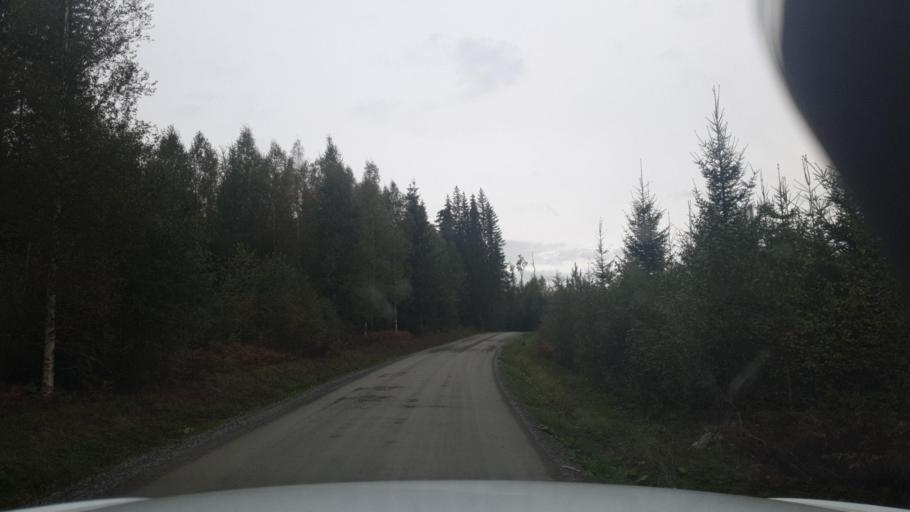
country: SE
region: Vaermland
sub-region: Karlstads Kommun
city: Edsvalla
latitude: 59.5881
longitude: 13.0758
